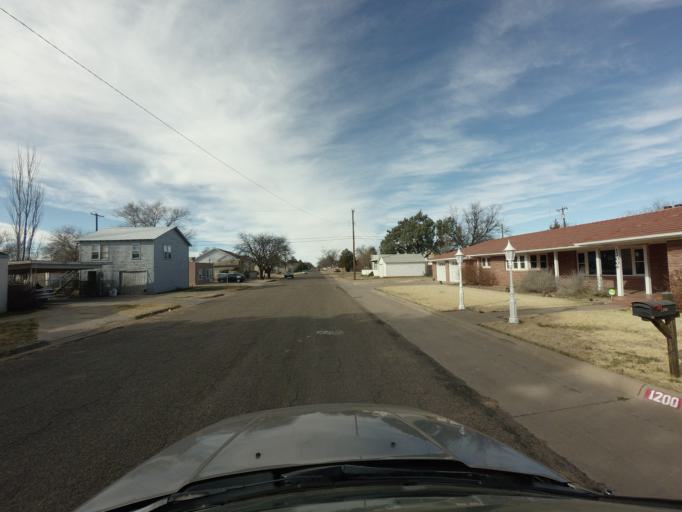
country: US
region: New Mexico
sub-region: Curry County
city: Clovis
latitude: 34.4099
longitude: -103.1992
